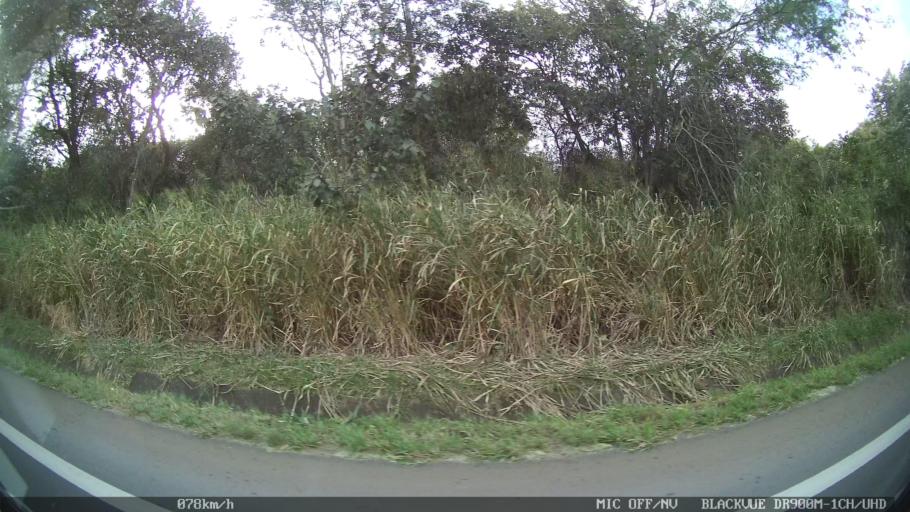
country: BR
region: Sao Paulo
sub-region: Cosmopolis
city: Cosmopolis
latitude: -22.6325
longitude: -47.3023
